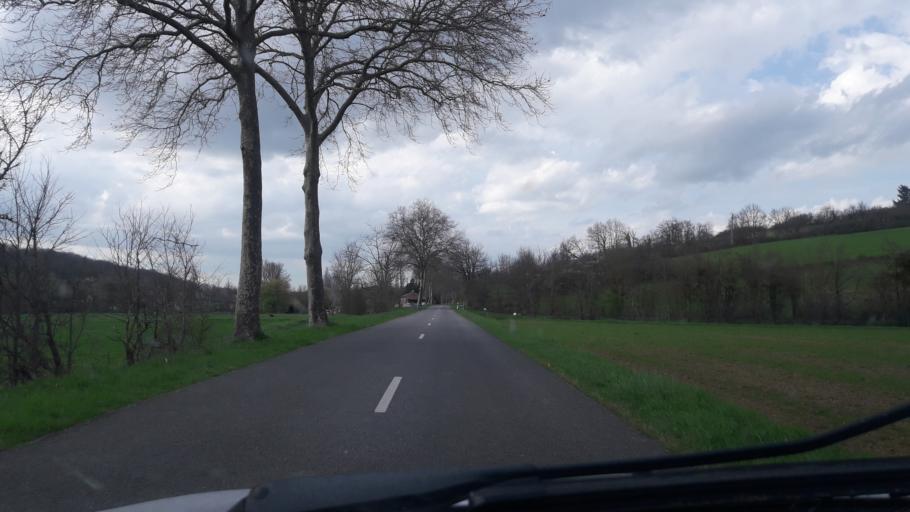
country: FR
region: Midi-Pyrenees
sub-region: Departement de la Haute-Garonne
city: Montesquieu-Volvestre
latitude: 43.2489
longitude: 1.2548
